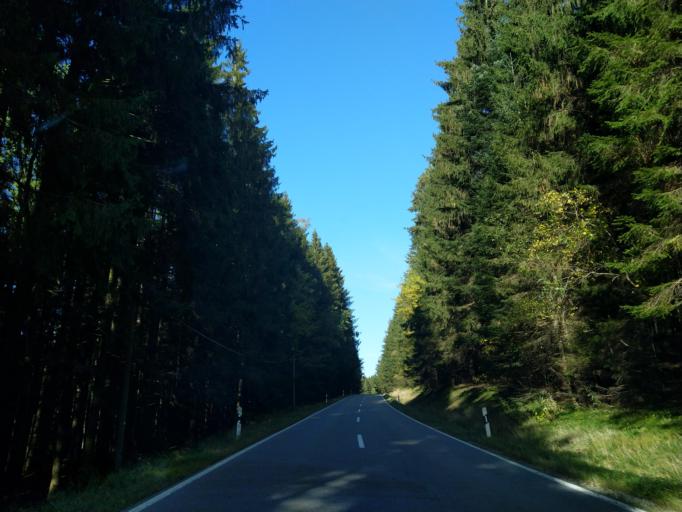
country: DE
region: Bavaria
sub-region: Lower Bavaria
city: Achslach
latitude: 48.9621
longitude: 12.9278
